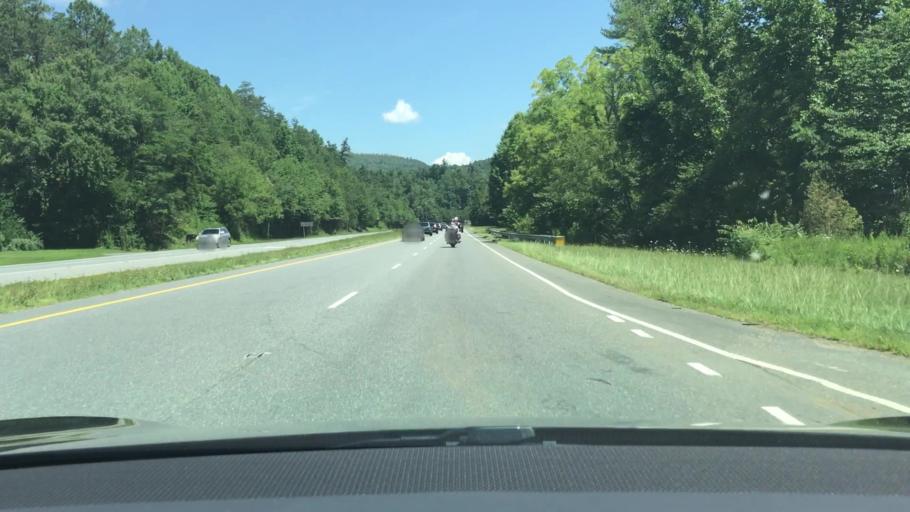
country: US
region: North Carolina
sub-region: Jackson County
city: Sylva
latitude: 35.3231
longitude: -83.2620
